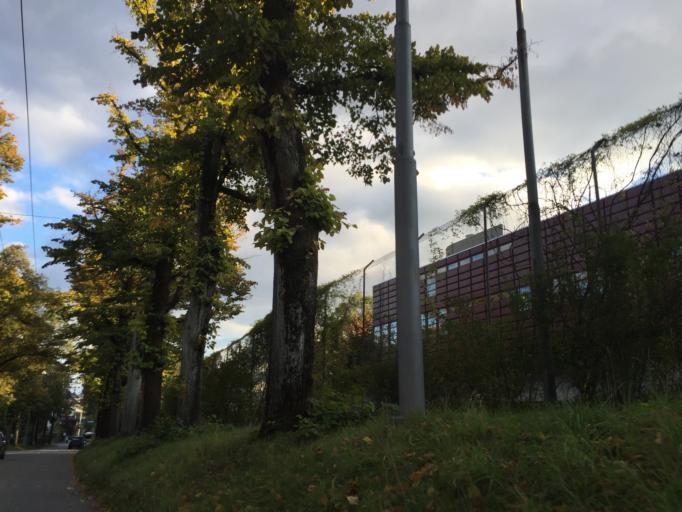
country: CH
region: Bern
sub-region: Bern-Mittelland District
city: Bern
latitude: 46.9601
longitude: 7.4348
